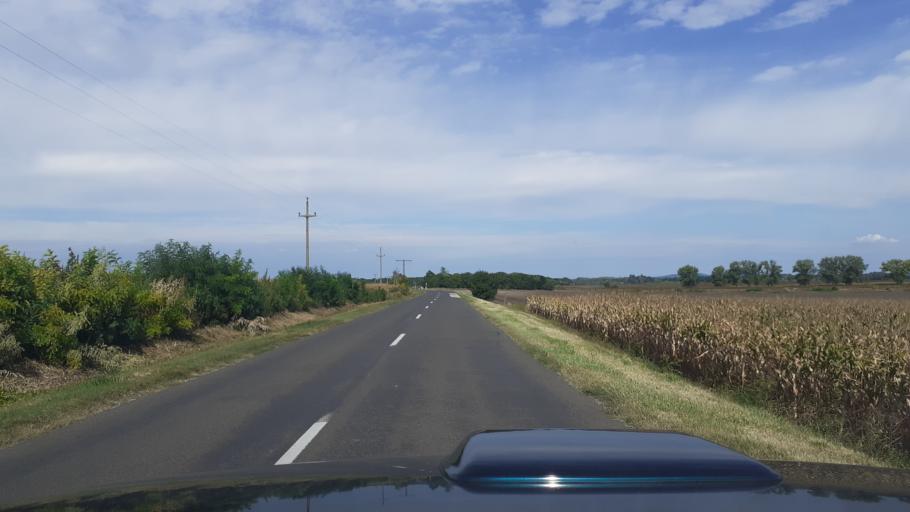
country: HU
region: Fejer
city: Pusztaszabolcs
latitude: 47.1215
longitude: 18.6901
